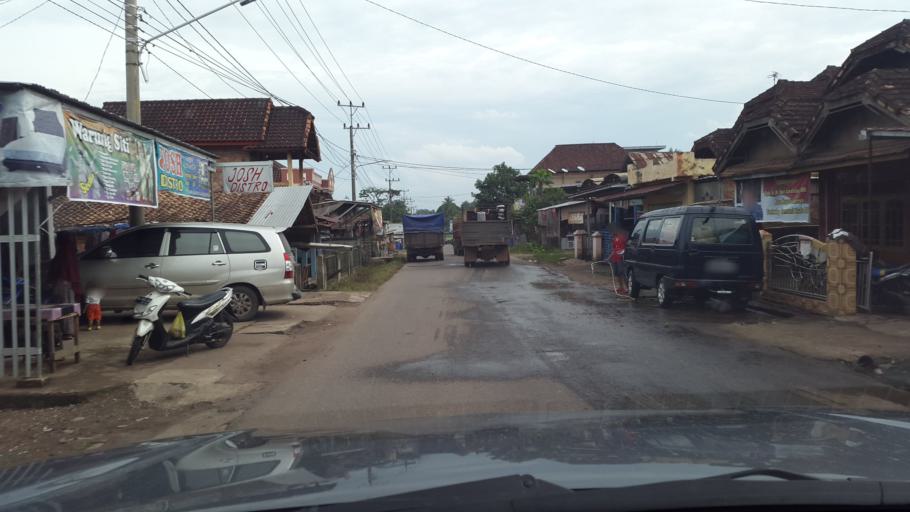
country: ID
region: South Sumatra
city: Gunungmegang Dalam
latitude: -3.4051
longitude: 103.9653
